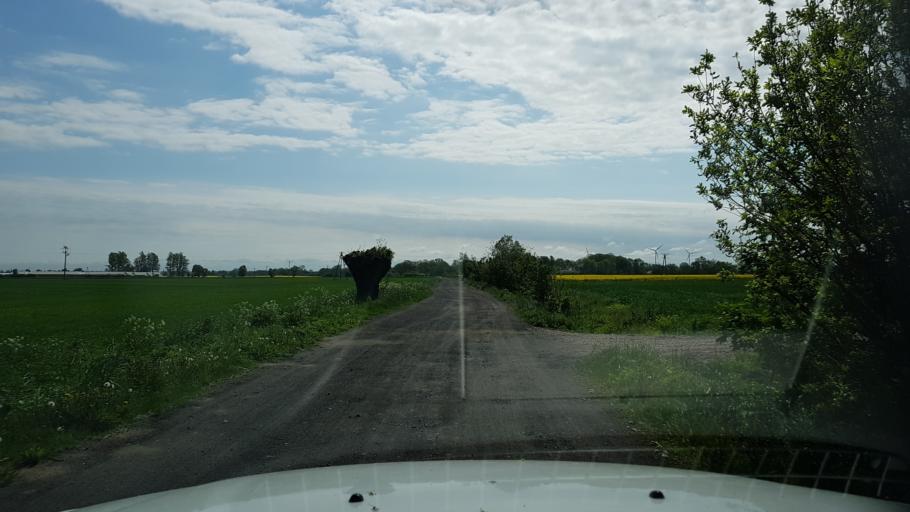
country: PL
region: West Pomeranian Voivodeship
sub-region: Powiat kolobrzeski
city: Ustronie Morskie
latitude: 54.2160
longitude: 15.8363
